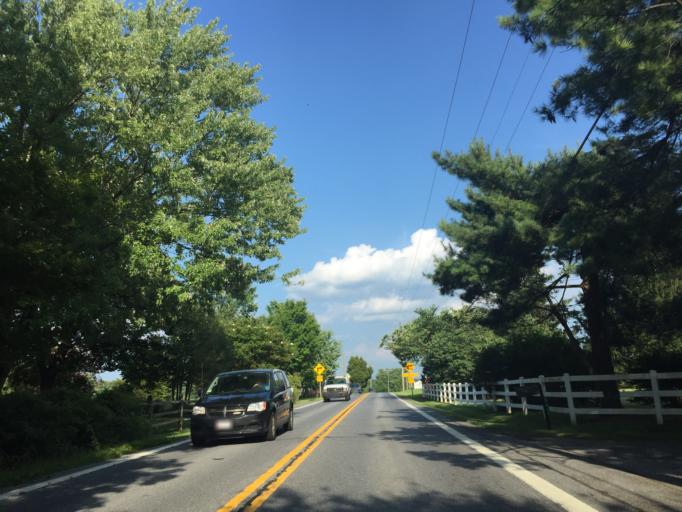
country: US
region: Maryland
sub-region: Carroll County
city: Hampstead
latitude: 39.5936
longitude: -76.7380
